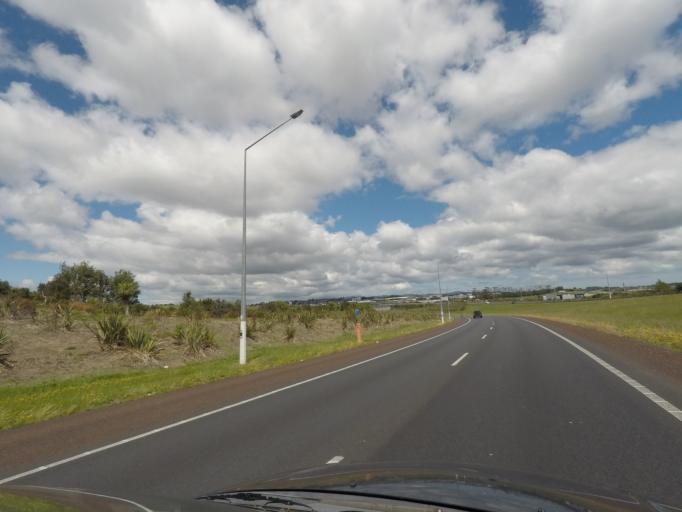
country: NZ
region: Auckland
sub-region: Auckland
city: Rosebank
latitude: -36.8114
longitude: 174.6159
